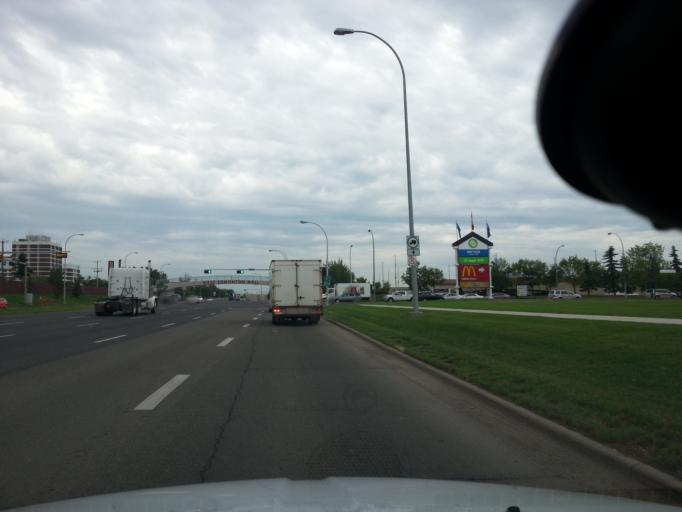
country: CA
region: Alberta
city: St. Albert
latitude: 53.5256
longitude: -113.6156
